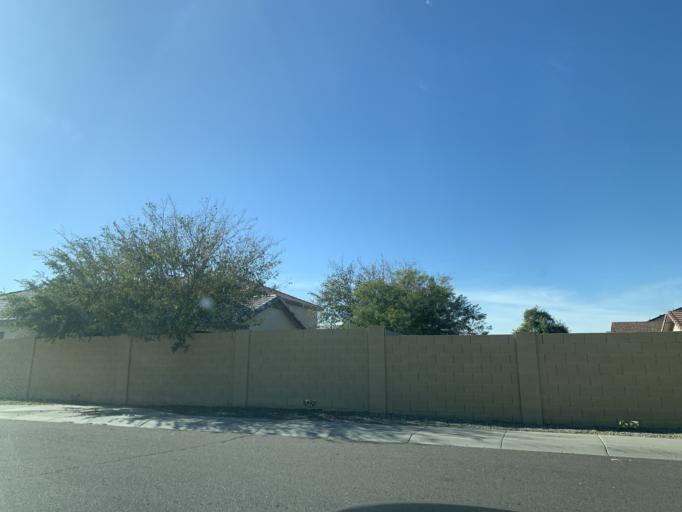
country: US
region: Arizona
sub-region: Maricopa County
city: Laveen
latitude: 33.3984
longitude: -112.1228
